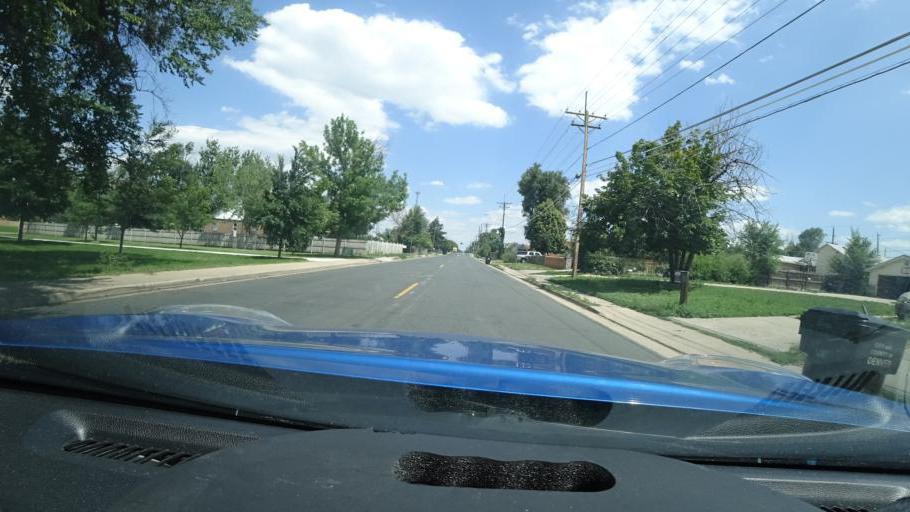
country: US
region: Colorado
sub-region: Jefferson County
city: Lakewood
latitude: 39.7004
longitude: -105.0506
